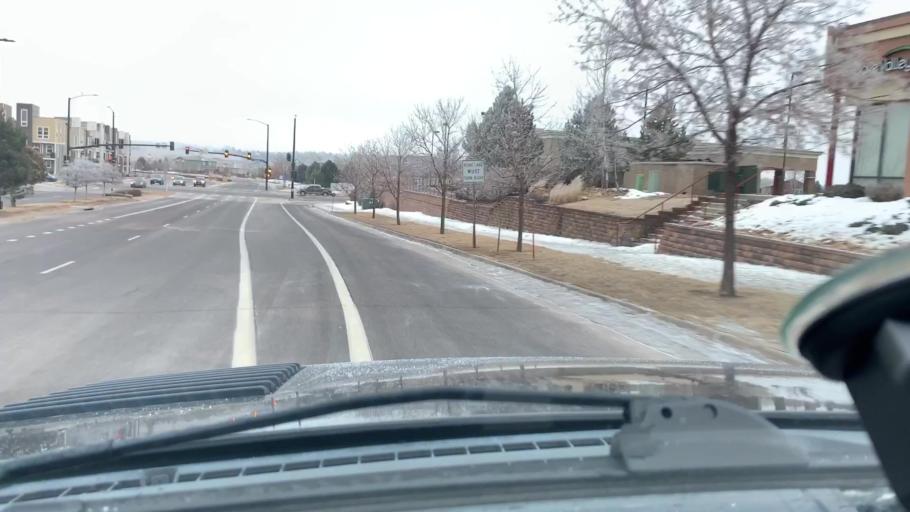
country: US
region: Colorado
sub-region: Arapahoe County
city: Dove Valley
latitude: 39.5757
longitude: -104.8084
